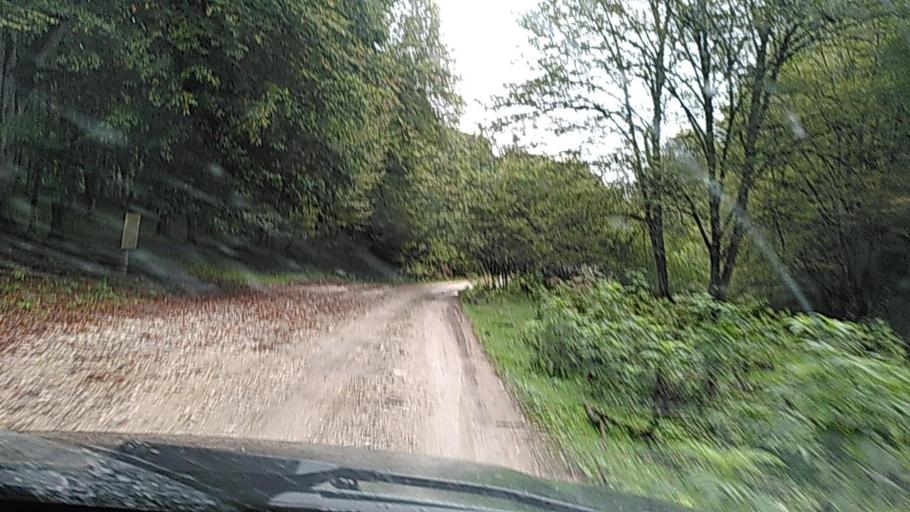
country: RU
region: Kabardino-Balkariya
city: Belaya Rechka
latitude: 43.4081
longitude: 43.4672
